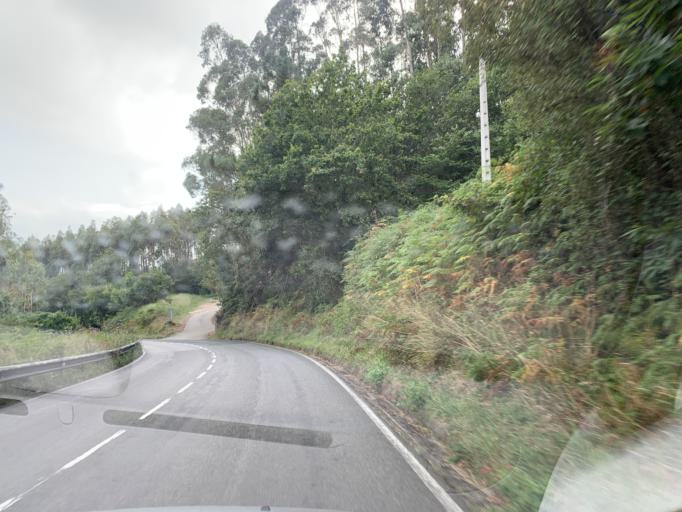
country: ES
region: Asturias
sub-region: Province of Asturias
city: Villaviciosa
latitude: 43.5078
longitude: -5.4270
